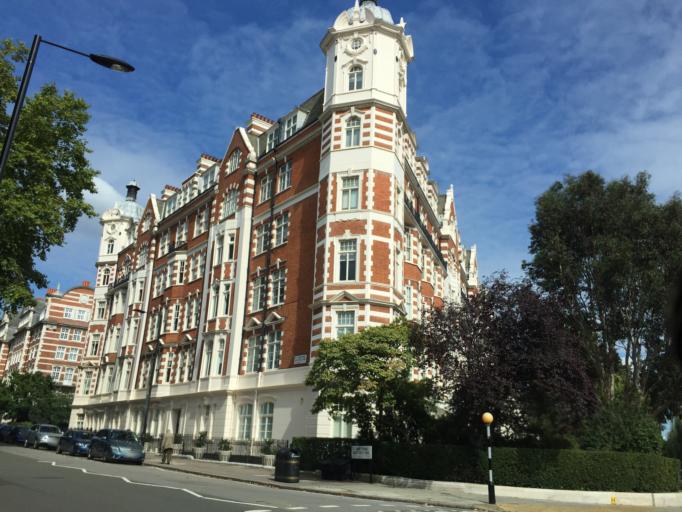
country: GB
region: England
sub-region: Greater London
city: Belsize Park
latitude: 51.5308
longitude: -0.1675
